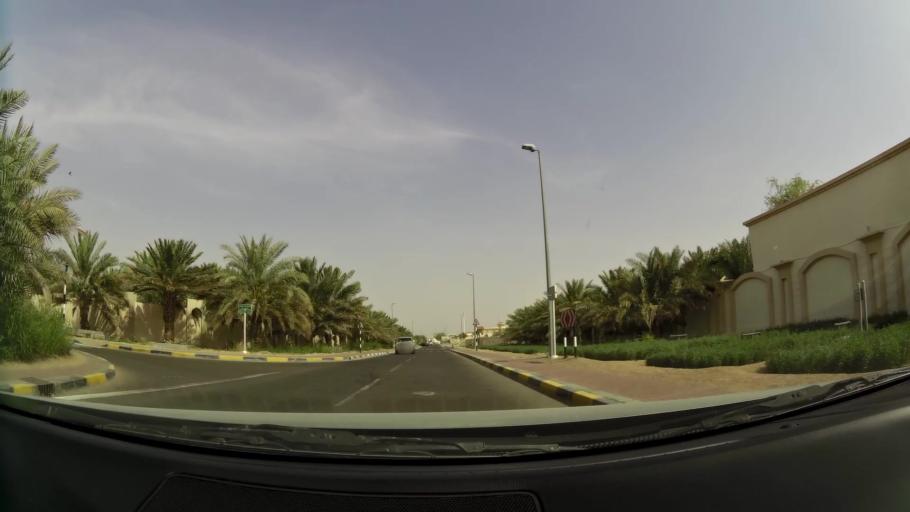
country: AE
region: Abu Dhabi
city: Al Ain
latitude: 24.1547
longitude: 55.6899
